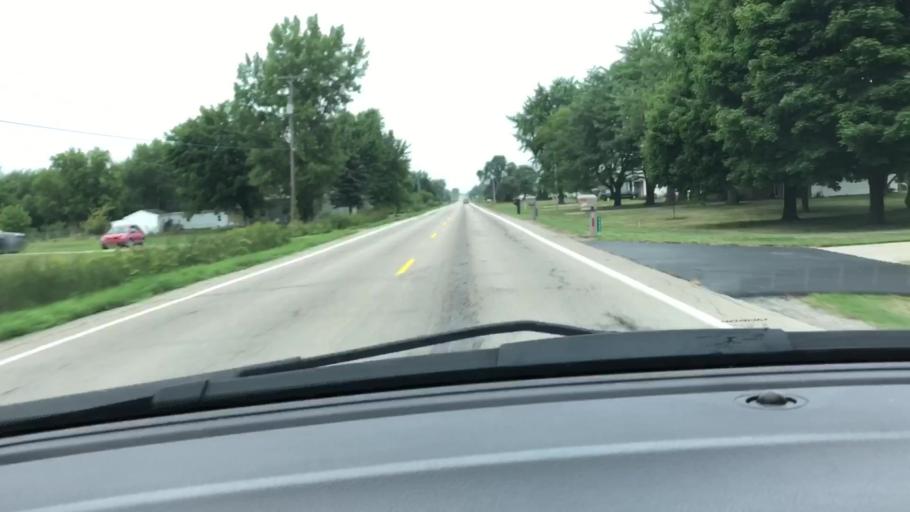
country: US
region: Michigan
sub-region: Bay County
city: Auburn
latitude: 43.5845
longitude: -84.0897
